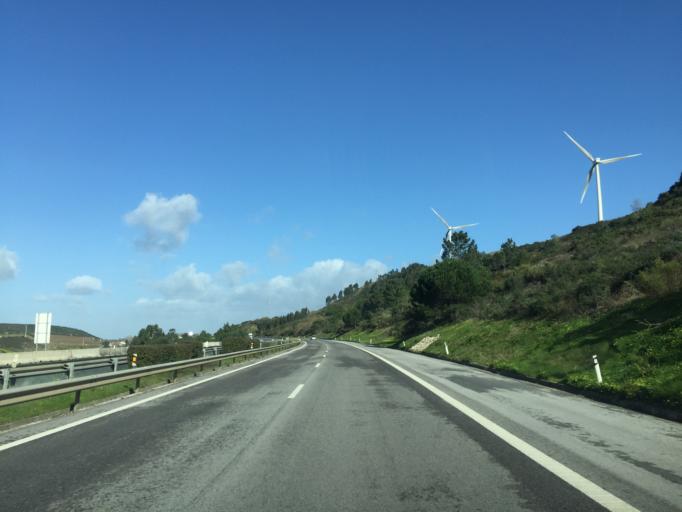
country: PT
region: Lisbon
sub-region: Torres Vedras
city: Torres Vedras
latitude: 39.0474
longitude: -9.2374
